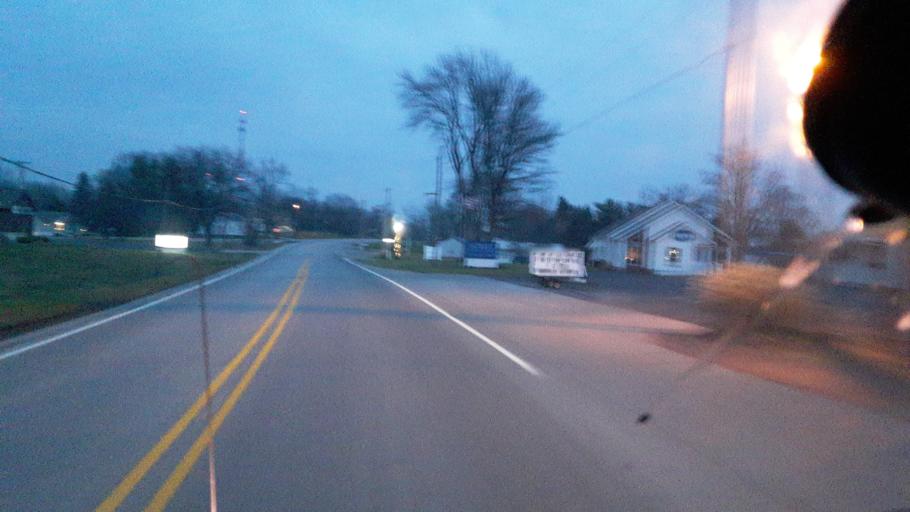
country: US
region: Indiana
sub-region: LaGrange County
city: Lagrange
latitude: 41.6345
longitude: -85.4175
